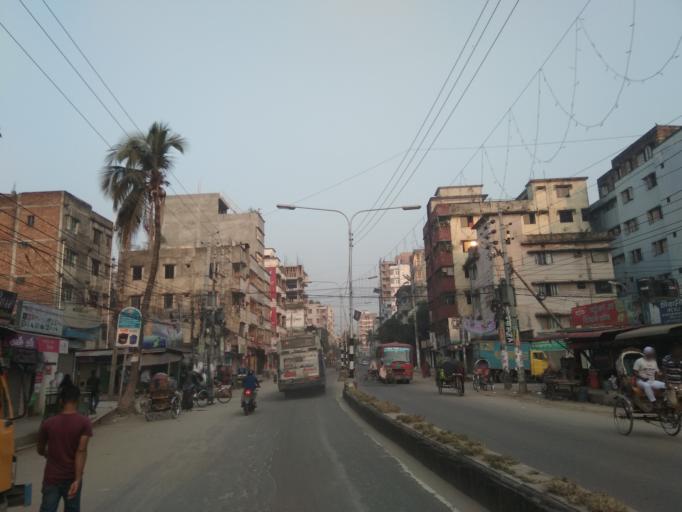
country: BD
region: Dhaka
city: Tungi
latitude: 23.8151
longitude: 90.3630
